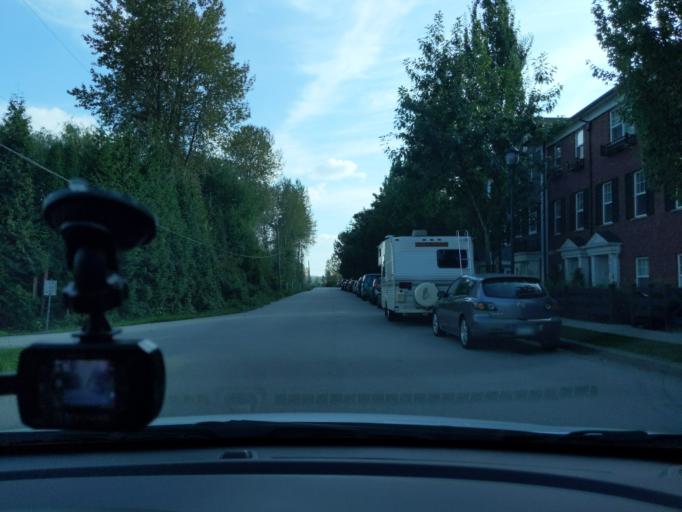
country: CA
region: British Columbia
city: Pitt Meadows
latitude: 49.2022
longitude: -122.6783
